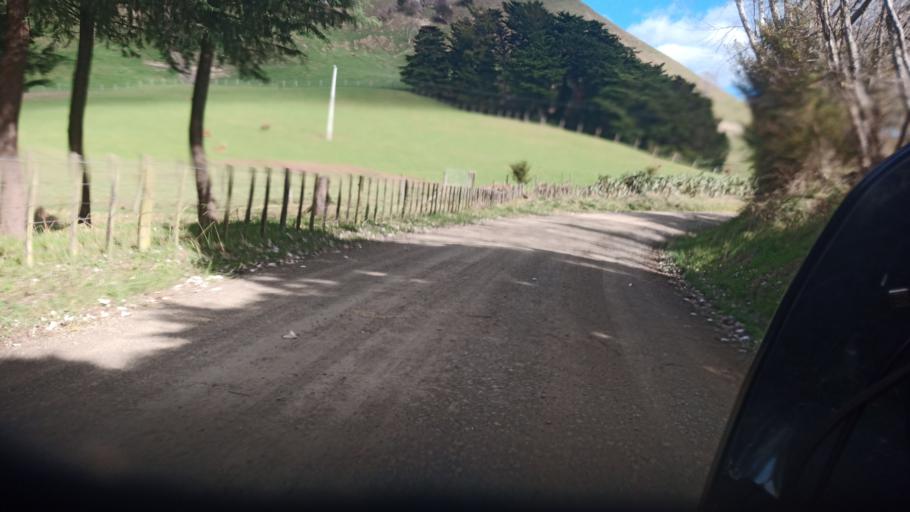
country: NZ
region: Gisborne
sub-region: Gisborne District
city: Gisborne
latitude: -38.4194
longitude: 177.7021
